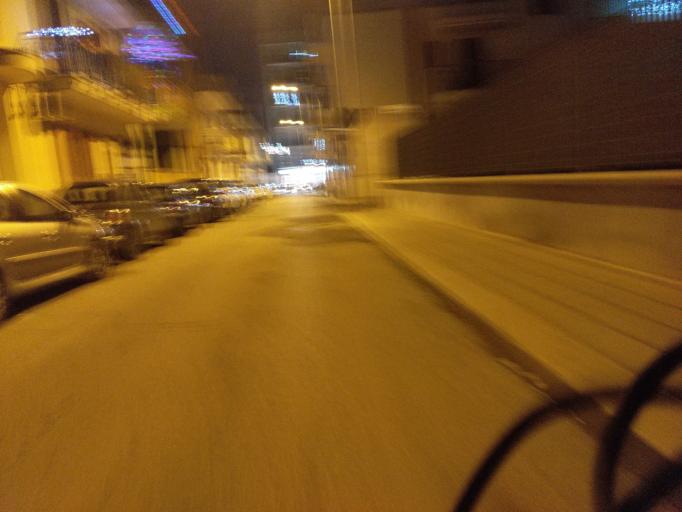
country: IT
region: Apulia
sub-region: Provincia di Bari
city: Modugno
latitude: 41.0859
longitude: 16.7878
